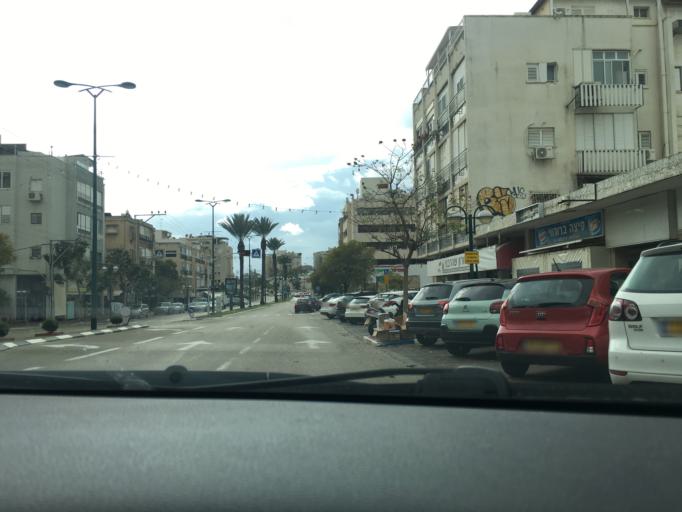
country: IL
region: Tel Aviv
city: Ramat HaSharon
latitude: 32.1395
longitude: 34.8420
